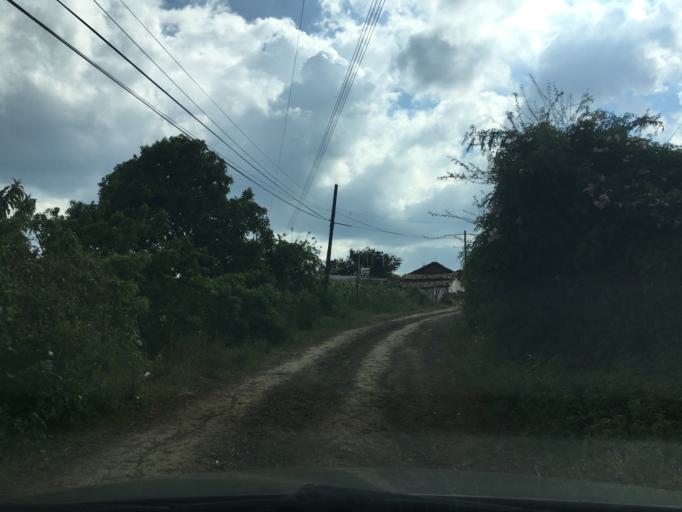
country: MX
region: Mexico
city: El Guayabito
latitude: 19.9015
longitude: -102.4987
